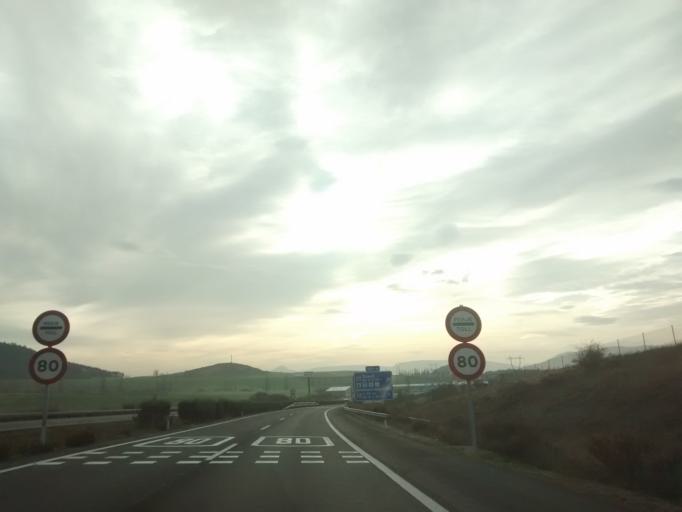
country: ES
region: Navarre
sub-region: Provincia de Navarra
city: Oltza
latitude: 42.8722
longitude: -1.7521
